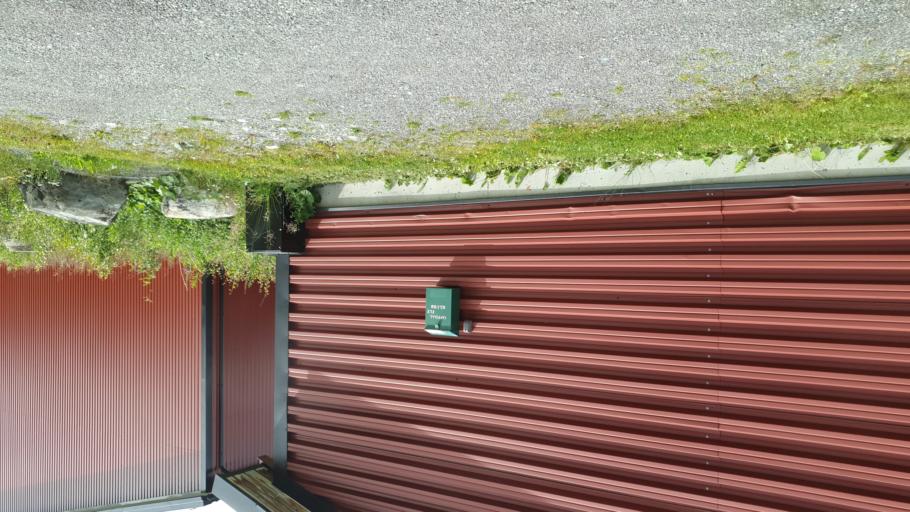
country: NO
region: Sor-Trondelag
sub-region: Oppdal
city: Oppdal
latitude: 62.6501
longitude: 9.8541
